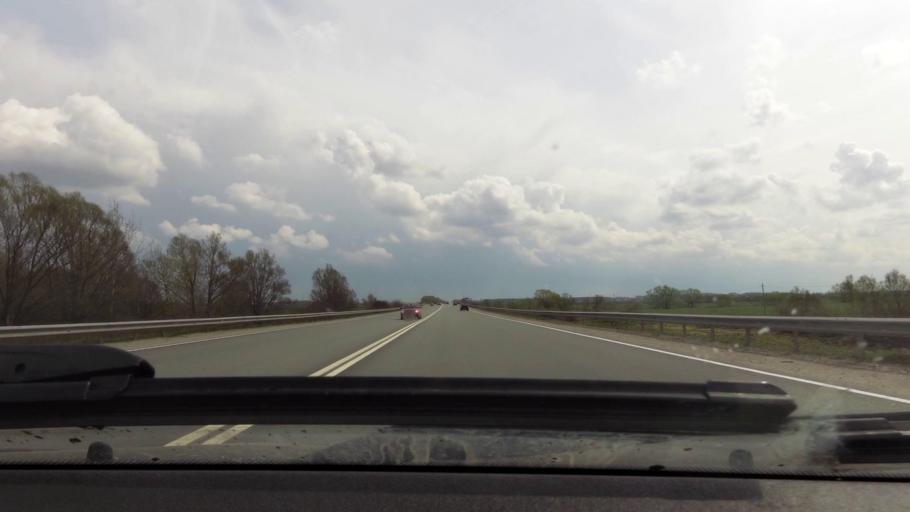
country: RU
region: Rjazan
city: Bagramovo
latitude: 54.7455
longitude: 39.4344
